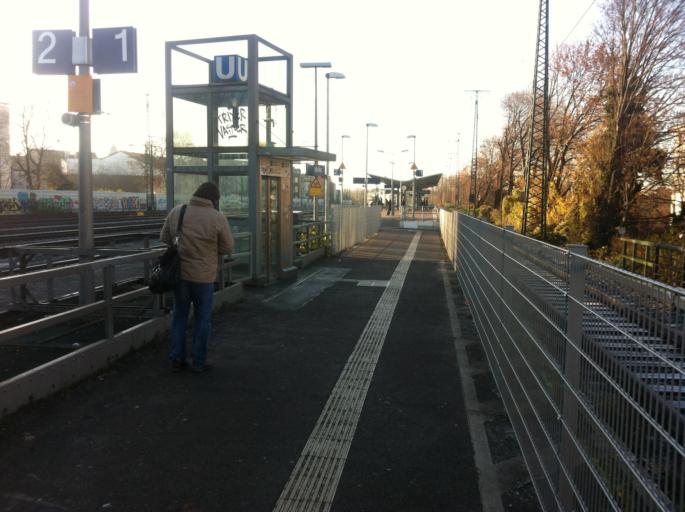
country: DE
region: North Rhine-Westphalia
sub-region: Regierungsbezirk Koln
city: Neuehrenfeld
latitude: 50.9433
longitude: 6.9337
